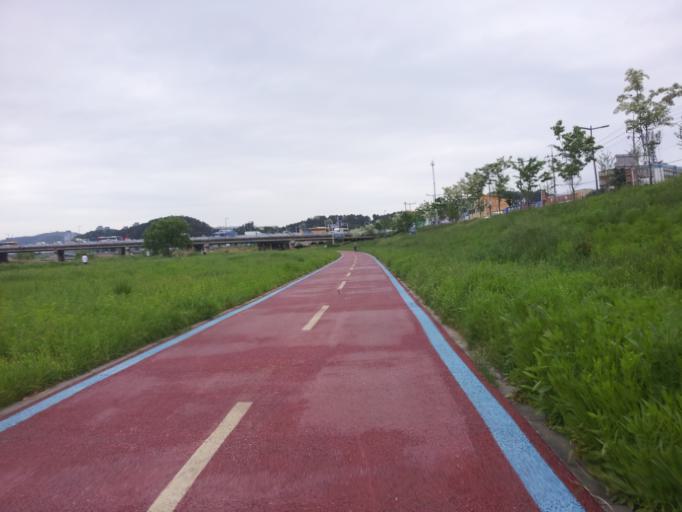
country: KR
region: Daejeon
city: Daejeon
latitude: 36.3545
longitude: 127.4050
